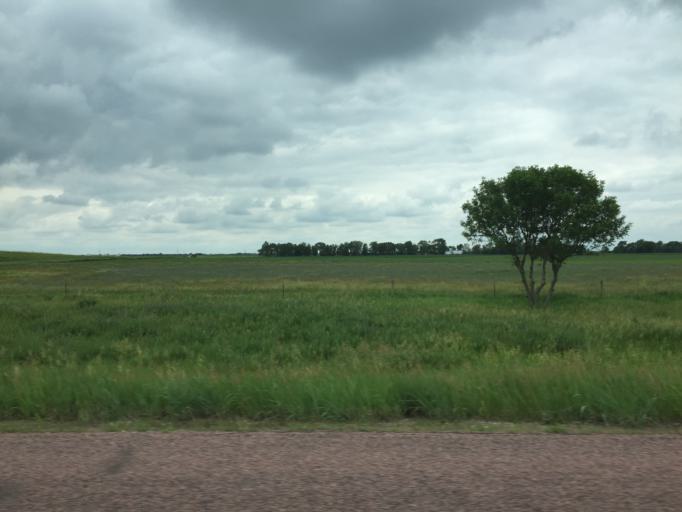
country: US
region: South Dakota
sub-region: Hanson County
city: Alexandria
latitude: 43.6656
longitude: -97.7286
